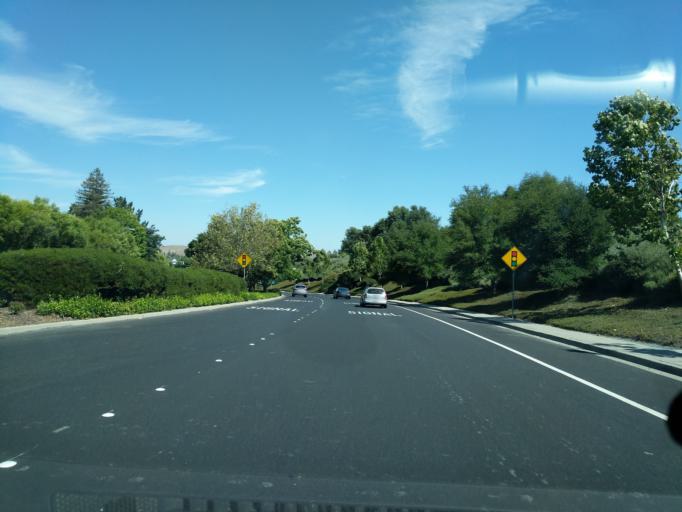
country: US
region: California
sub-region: Contra Costa County
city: San Ramon
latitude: 37.7592
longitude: -121.9703
